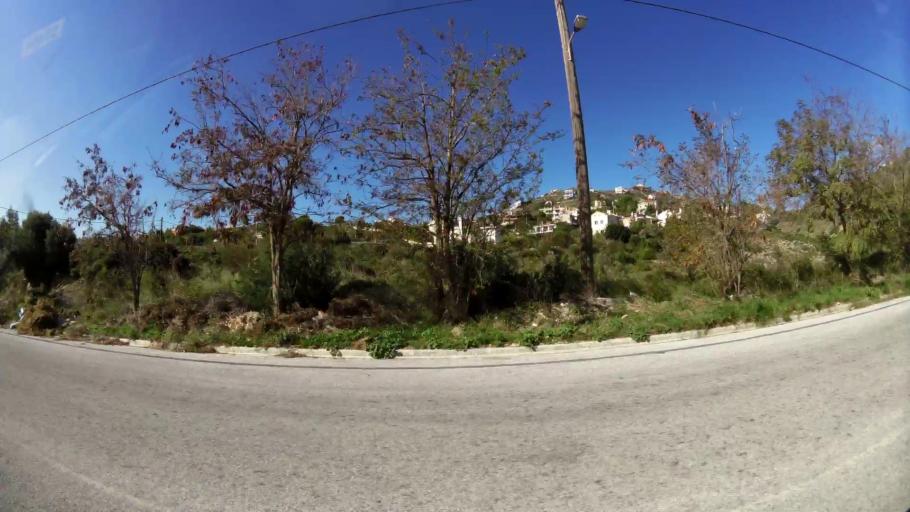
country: GR
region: Attica
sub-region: Nomarchia Anatolikis Attikis
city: Dhrafi
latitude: 38.0381
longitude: 23.9049
